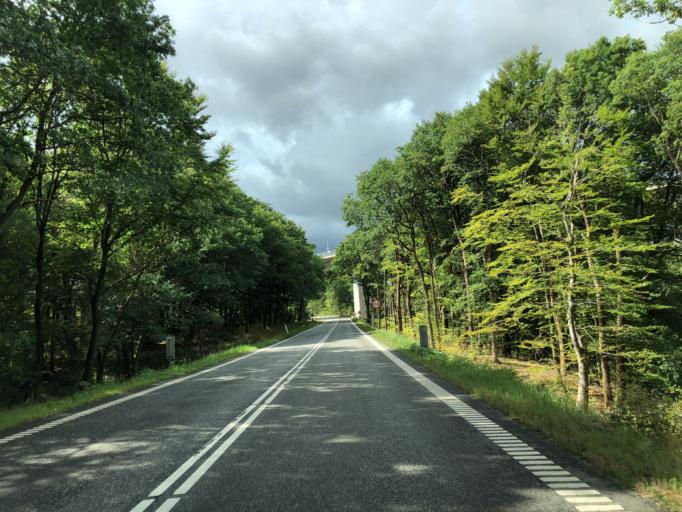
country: DK
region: Central Jutland
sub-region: Silkeborg Kommune
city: Silkeborg
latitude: 56.1386
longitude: 9.4060
